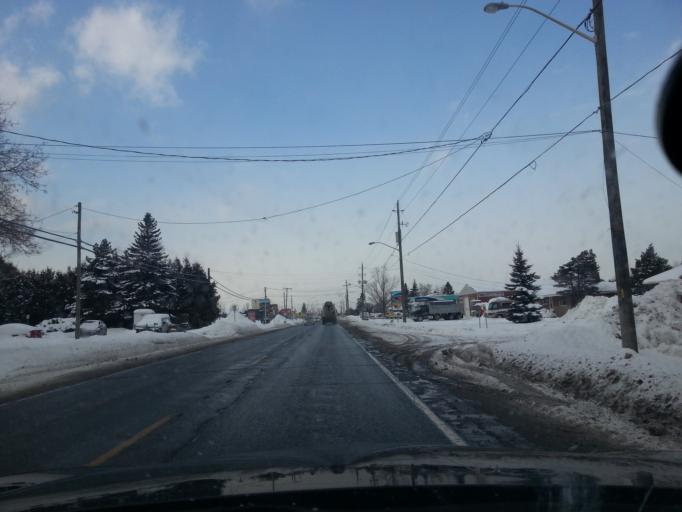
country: CA
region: Ontario
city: Bells Corners
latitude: 45.2744
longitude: -75.9487
